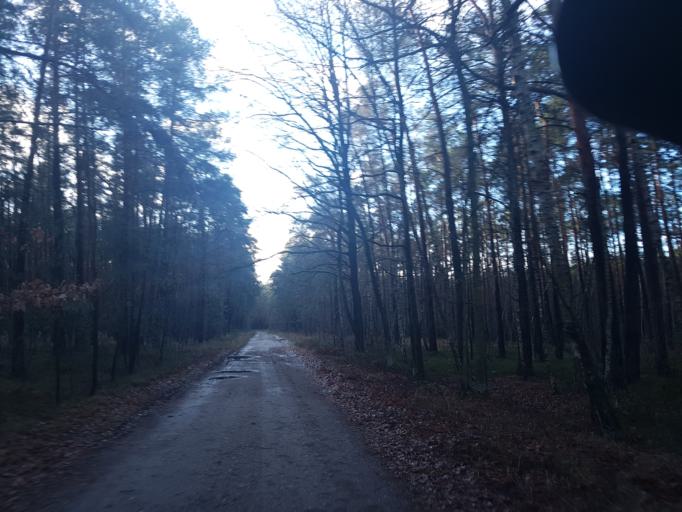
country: DE
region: Brandenburg
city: Ruckersdorf
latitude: 51.5896
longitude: 13.6023
